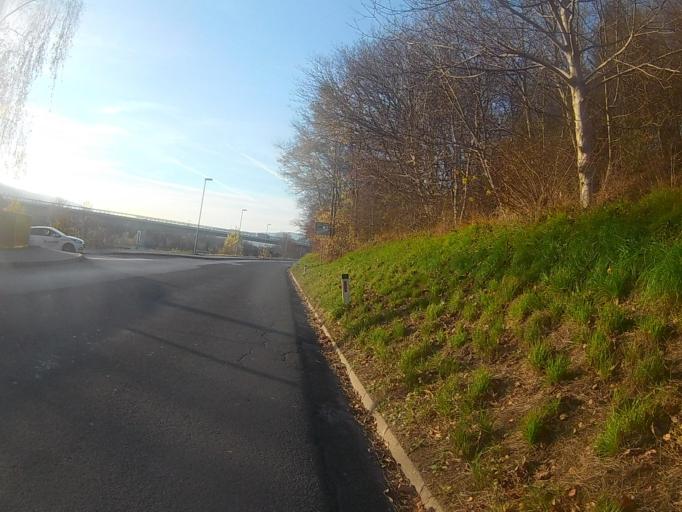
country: SI
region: Maribor
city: Maribor
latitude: 46.5560
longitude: 15.6937
